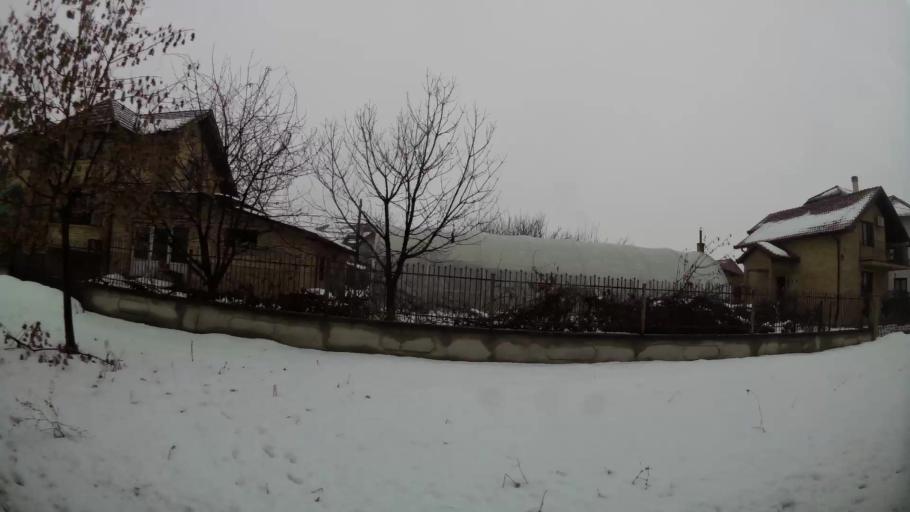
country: RS
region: Central Serbia
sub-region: Belgrade
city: Zemun
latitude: 44.8469
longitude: 20.3453
